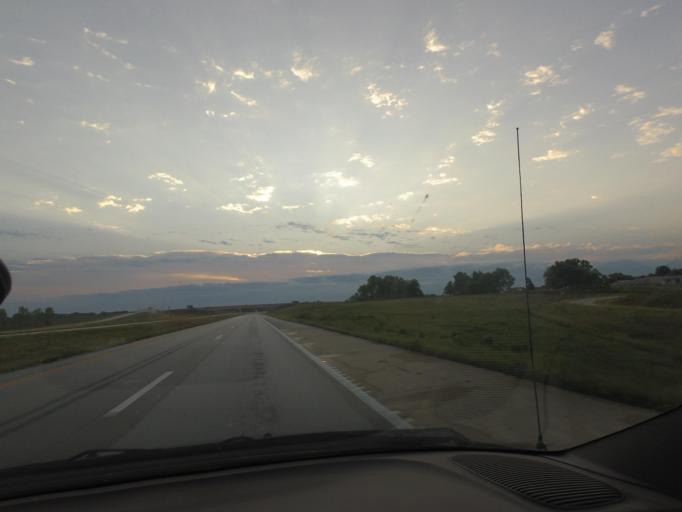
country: US
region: Missouri
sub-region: Macon County
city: Macon
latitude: 39.7517
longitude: -92.2621
